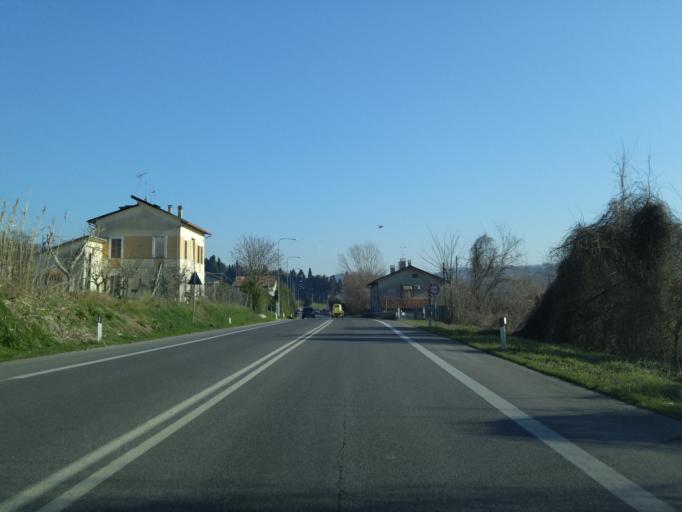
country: IT
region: The Marches
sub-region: Provincia di Pesaro e Urbino
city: Gradara
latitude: 43.9533
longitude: 12.7804
